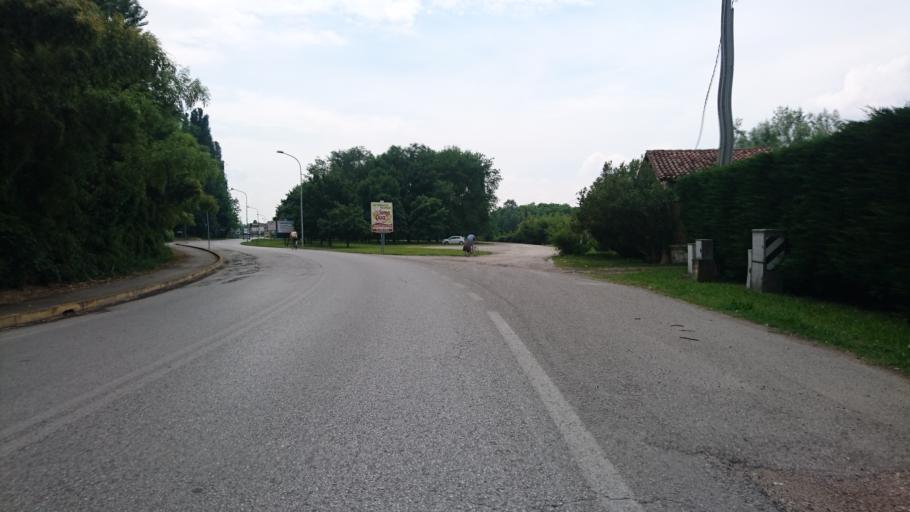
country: IT
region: Veneto
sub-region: Provincia di Rovigo
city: Badia Polesine
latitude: 45.0918
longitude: 11.4855
